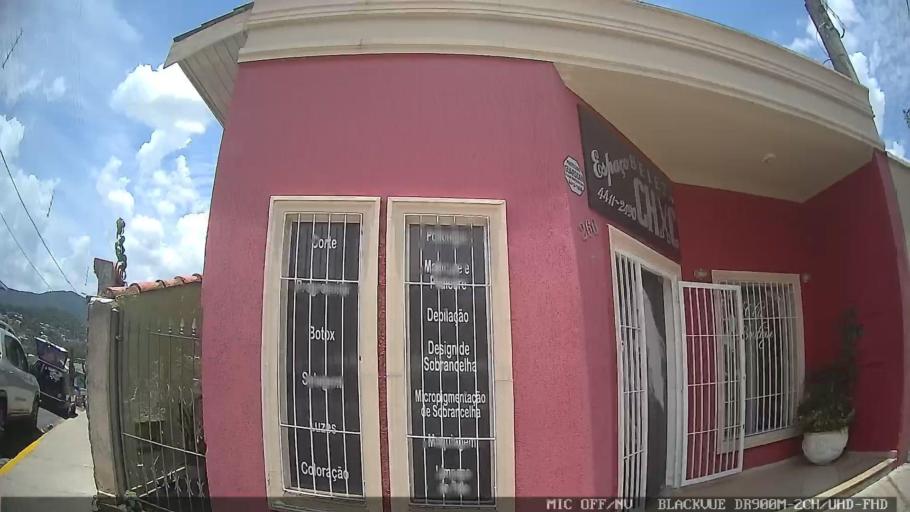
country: BR
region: Sao Paulo
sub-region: Atibaia
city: Atibaia
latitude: -23.1179
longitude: -46.5519
